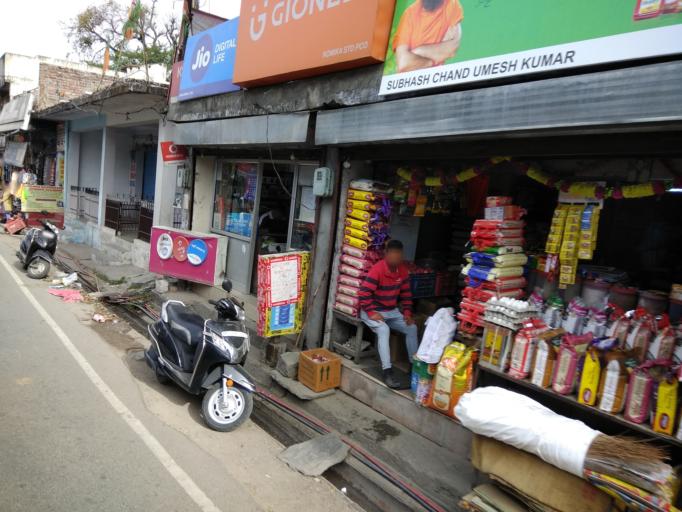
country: IN
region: Himachal Pradesh
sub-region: Kangra
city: Dharmsala
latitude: 32.1832
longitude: 76.3745
